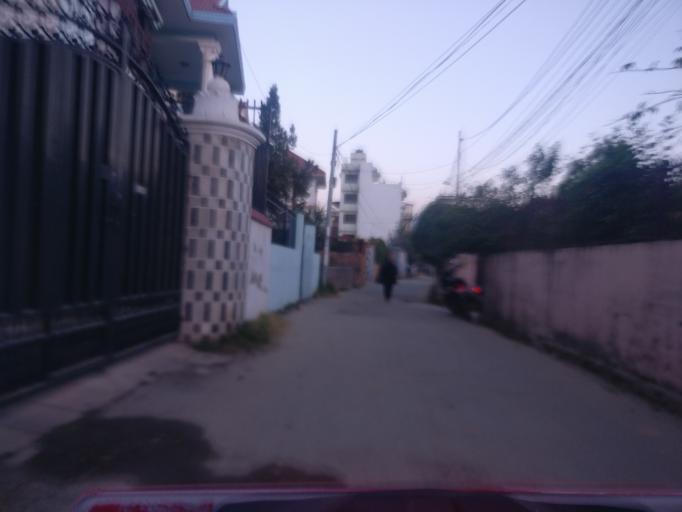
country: NP
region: Central Region
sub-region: Bagmati Zone
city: Patan
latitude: 27.6509
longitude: 85.3199
